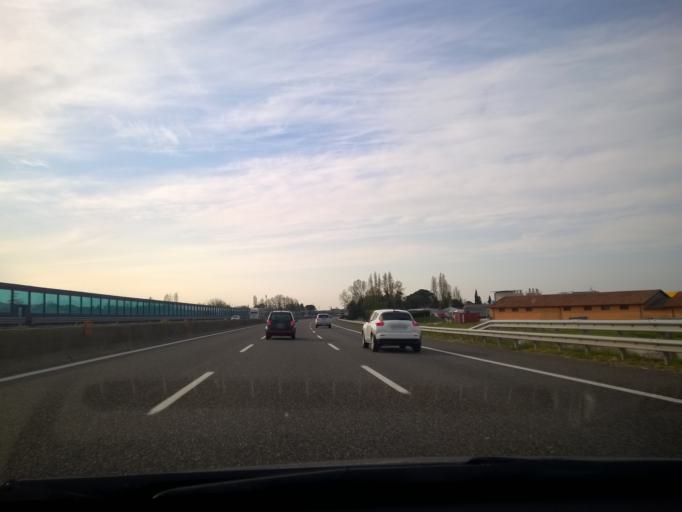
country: IT
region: Emilia-Romagna
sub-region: Forli-Cesena
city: San Mauro Pascoli
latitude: 44.1076
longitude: 12.4271
